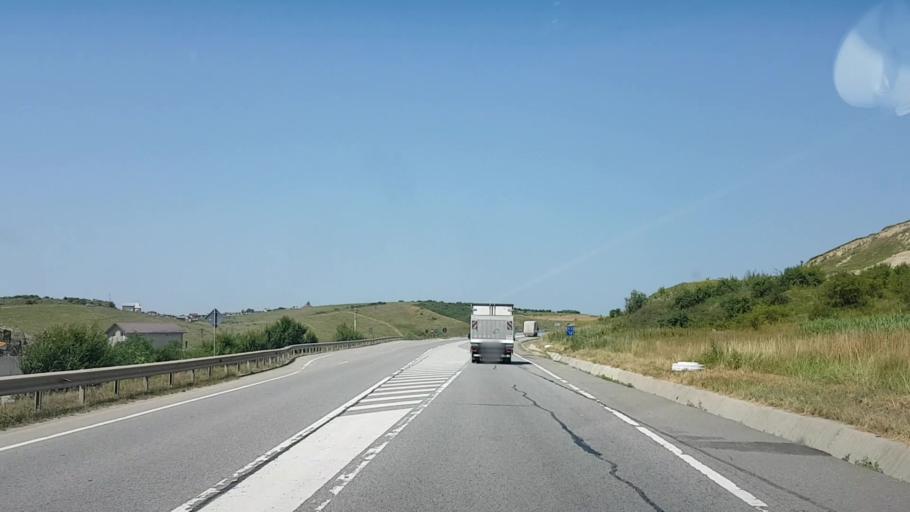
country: RO
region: Cluj
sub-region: Comuna Apahida
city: Dezmir
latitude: 46.7661
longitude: 23.6903
